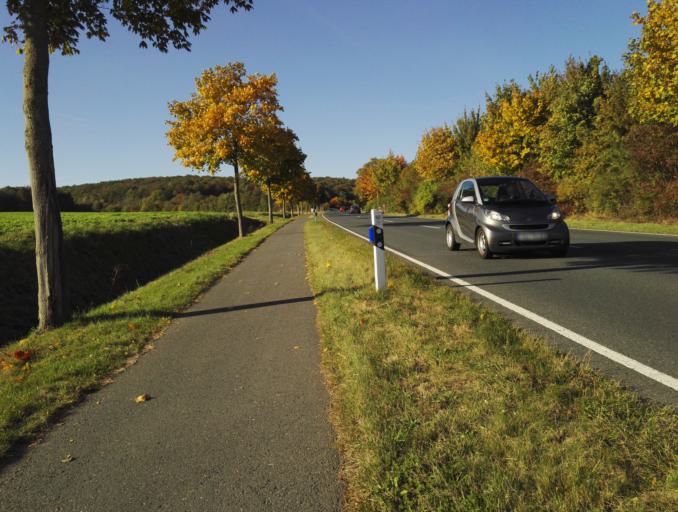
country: DE
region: Lower Saxony
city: Schellerten
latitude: 52.1188
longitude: 10.0986
